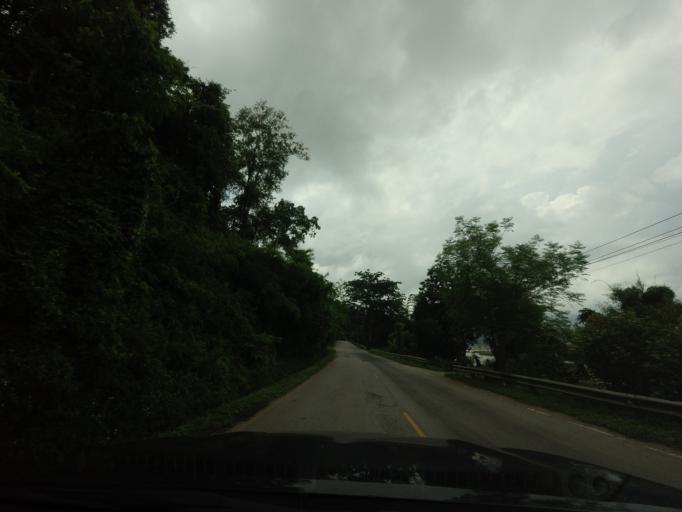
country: TH
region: Loei
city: Pak Chom
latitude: 18.0539
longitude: 101.8195
